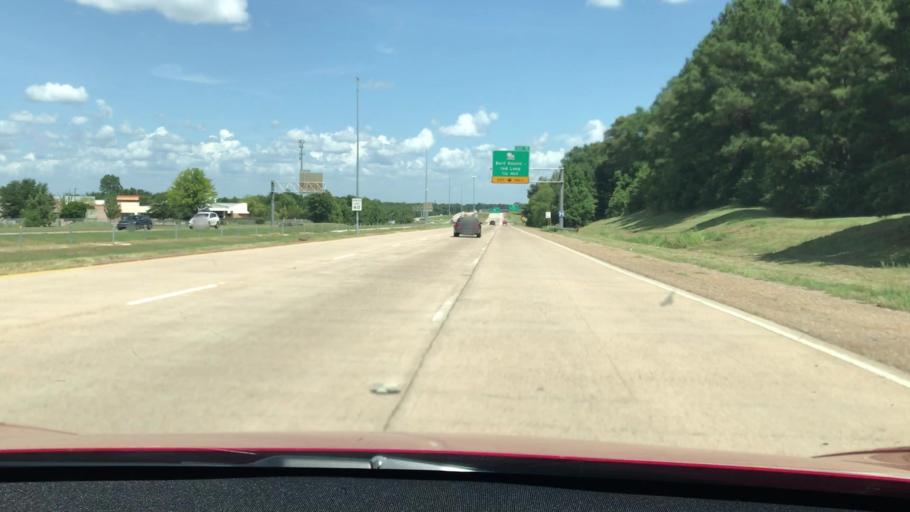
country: US
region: Louisiana
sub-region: Bossier Parish
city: Bossier City
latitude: 32.4143
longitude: -93.7333
